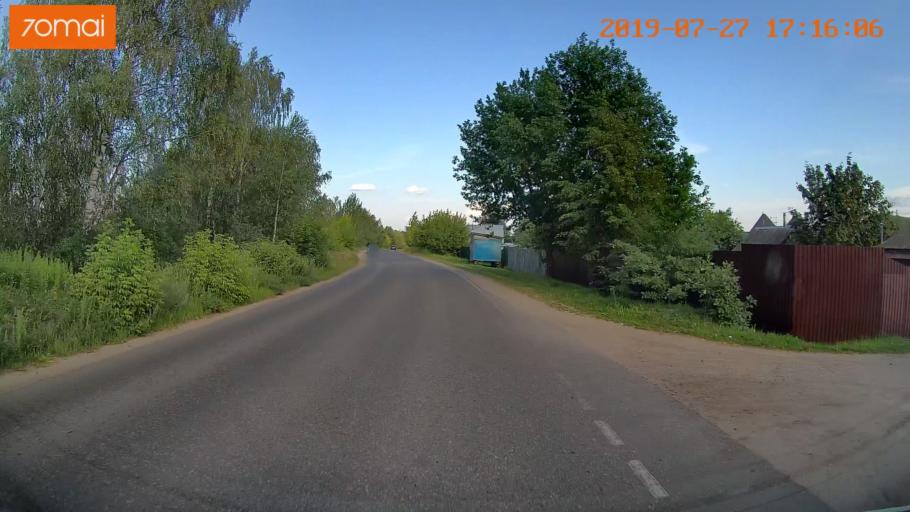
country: RU
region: Ivanovo
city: Novo-Talitsy
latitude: 57.0442
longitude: 40.8788
